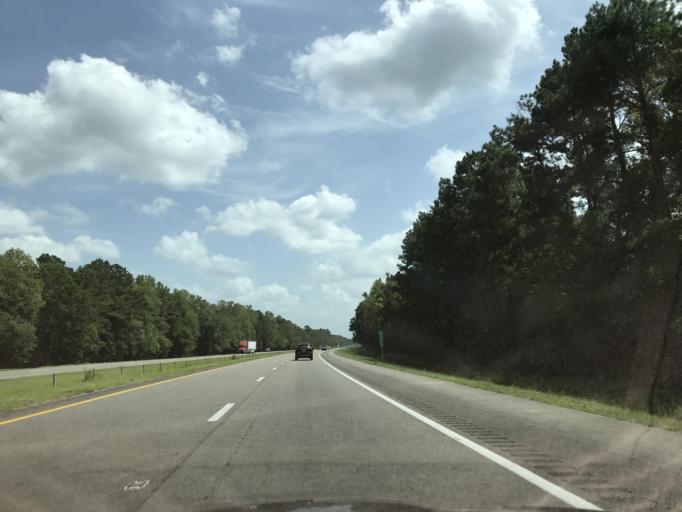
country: US
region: North Carolina
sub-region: Pender County
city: Burgaw
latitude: 34.6088
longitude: -77.9178
